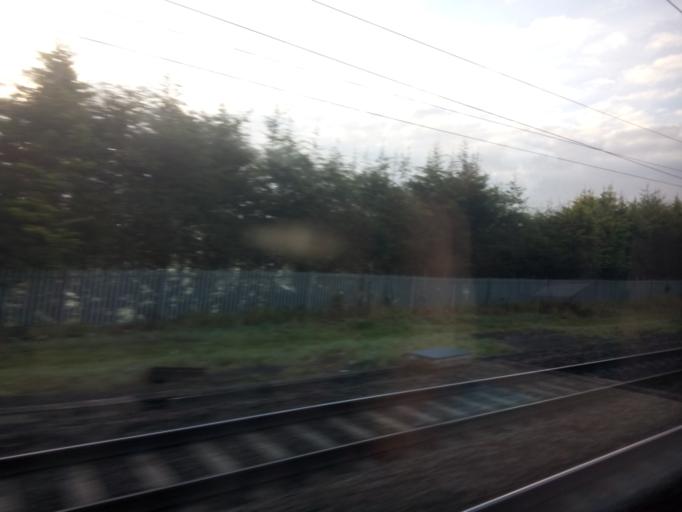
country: GB
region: England
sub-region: City of York
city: Bishopthorpe
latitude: 53.9407
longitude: -1.1118
